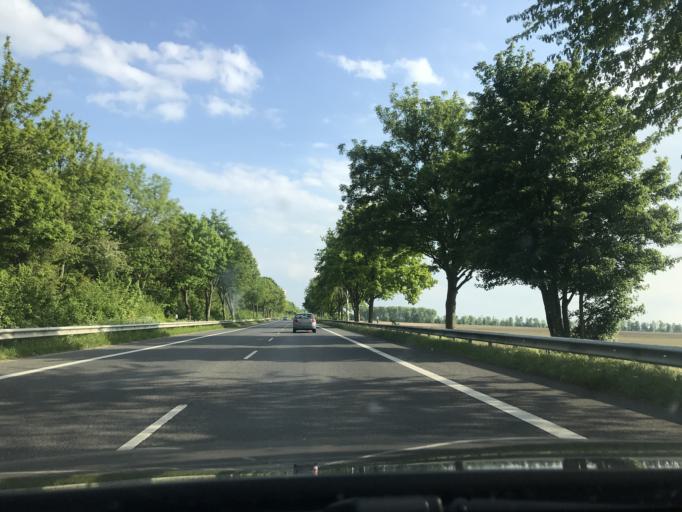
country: DE
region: North Rhine-Westphalia
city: Erkelenz
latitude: 51.0758
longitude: 6.2995
